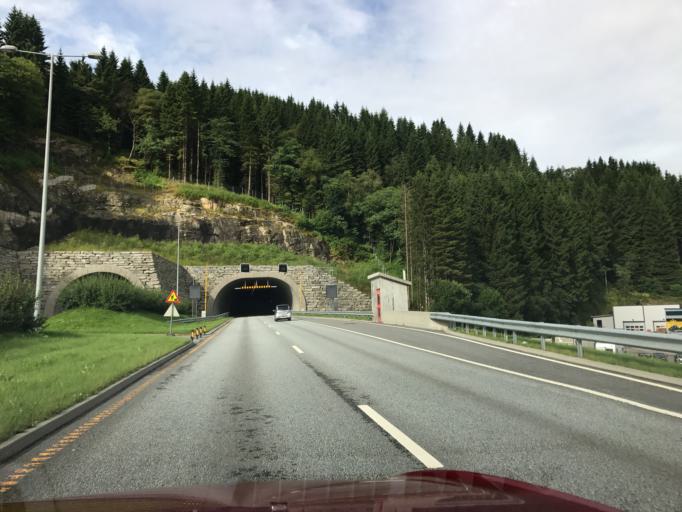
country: NO
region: Hordaland
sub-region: Bergen
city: Hylkje
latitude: 60.4804
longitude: 5.3676
